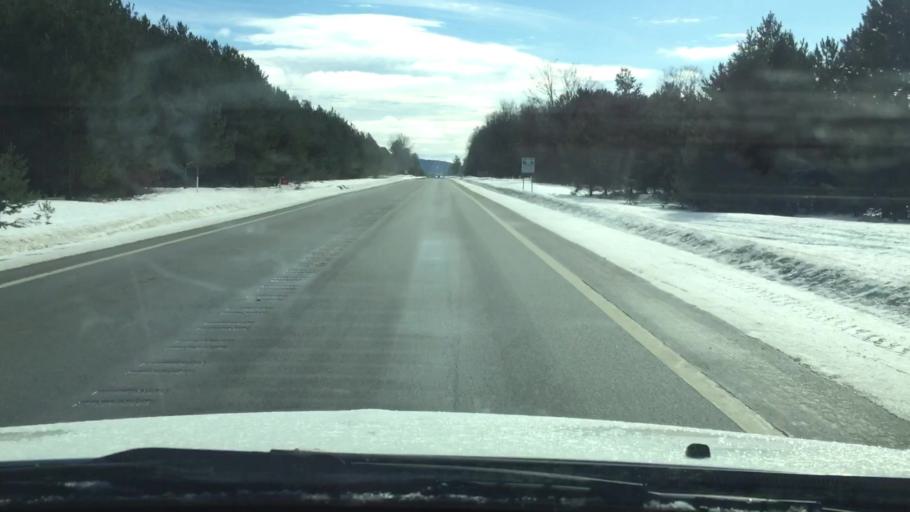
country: US
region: Michigan
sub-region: Antrim County
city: Mancelona
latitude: 44.9409
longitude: -85.0508
